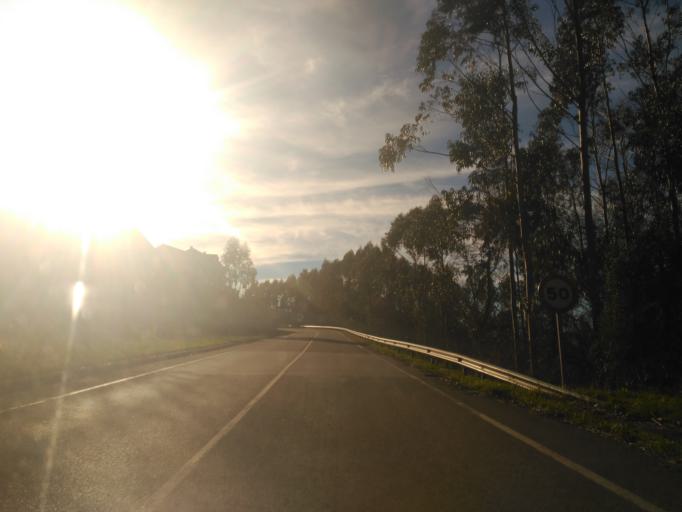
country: ES
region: Cantabria
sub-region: Provincia de Cantabria
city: Cabezon de la Sal
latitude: 43.3374
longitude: -4.2708
